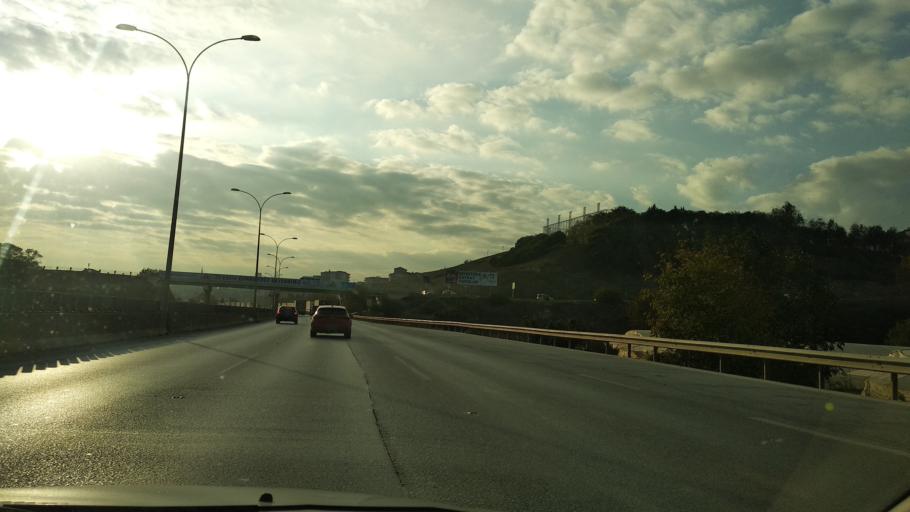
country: TR
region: Istanbul
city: Pendik
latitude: 40.8744
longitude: 29.2966
